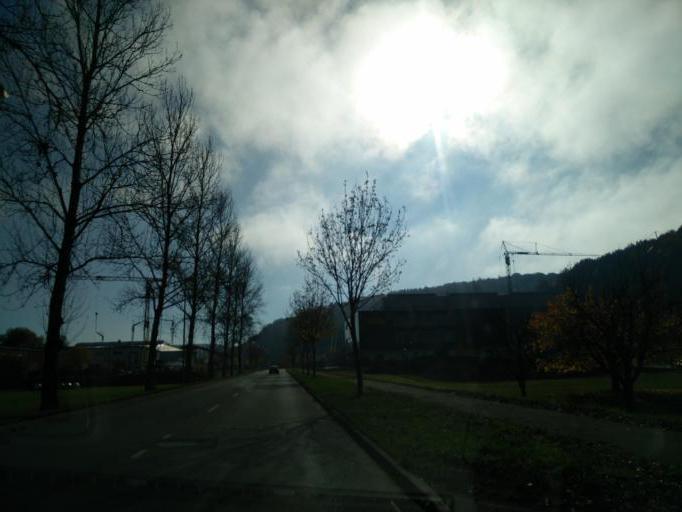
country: DE
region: Baden-Wuerttemberg
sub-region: Tuebingen Region
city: Tuebingen
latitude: 48.4970
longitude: 9.0594
